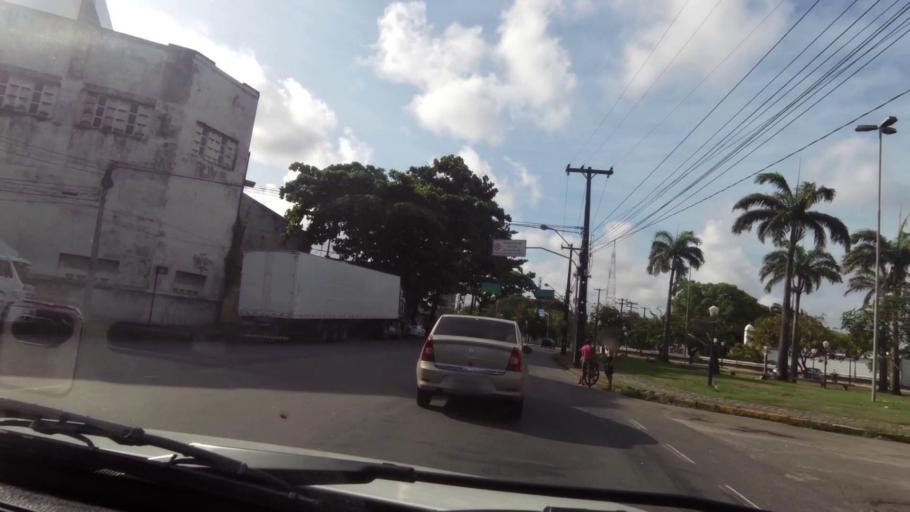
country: BR
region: Pernambuco
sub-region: Recife
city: Recife
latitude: -8.0516
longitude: -34.8706
